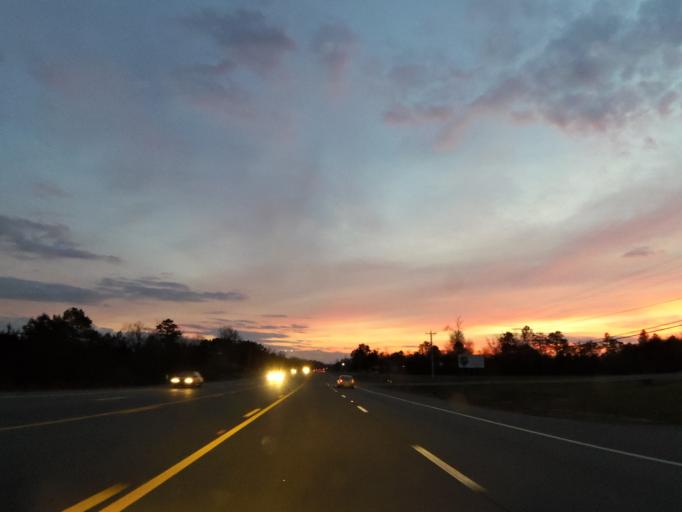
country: US
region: Tennessee
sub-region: Polk County
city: Benton
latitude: 35.1549
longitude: -84.7039
